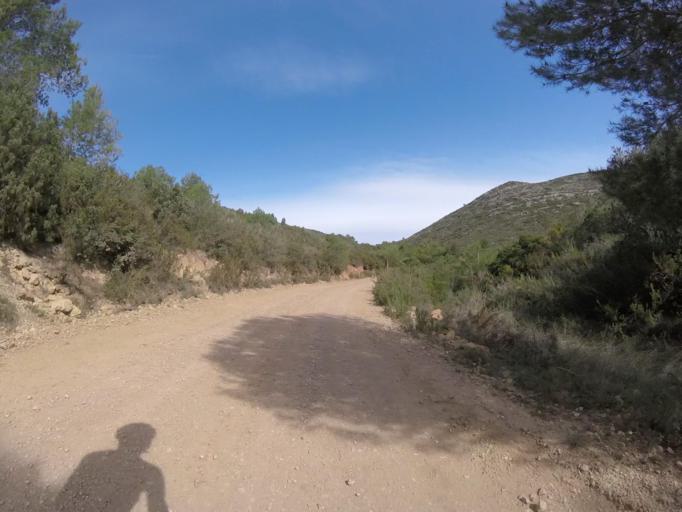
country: ES
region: Valencia
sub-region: Provincia de Castello
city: Torreblanca
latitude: 40.1994
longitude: 0.1540
